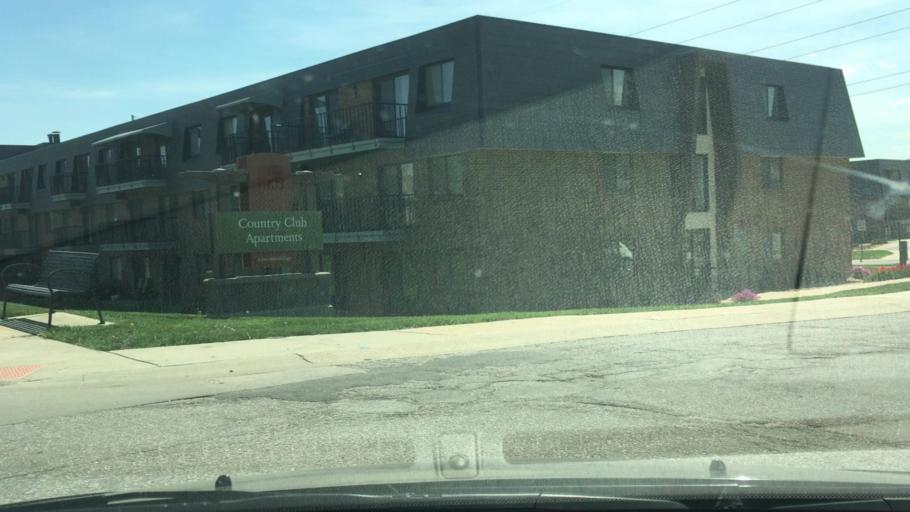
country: US
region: Missouri
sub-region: Jackson County
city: Lees Summit
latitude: 38.9241
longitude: -94.4109
